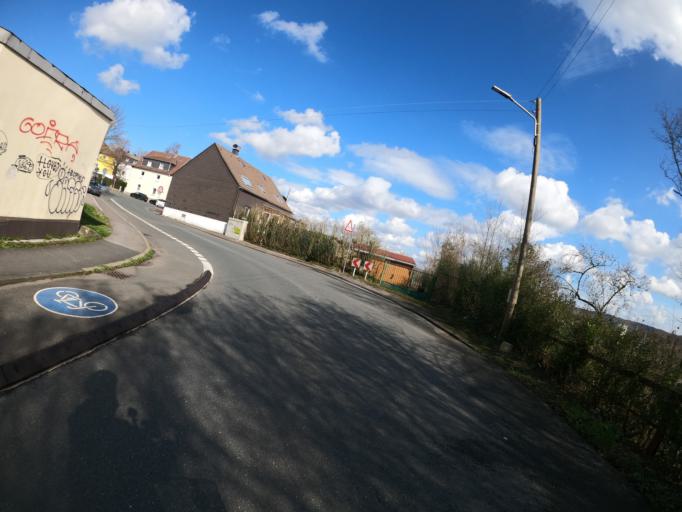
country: DE
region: North Rhine-Westphalia
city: Wulfrath
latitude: 51.2352
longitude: 7.0724
